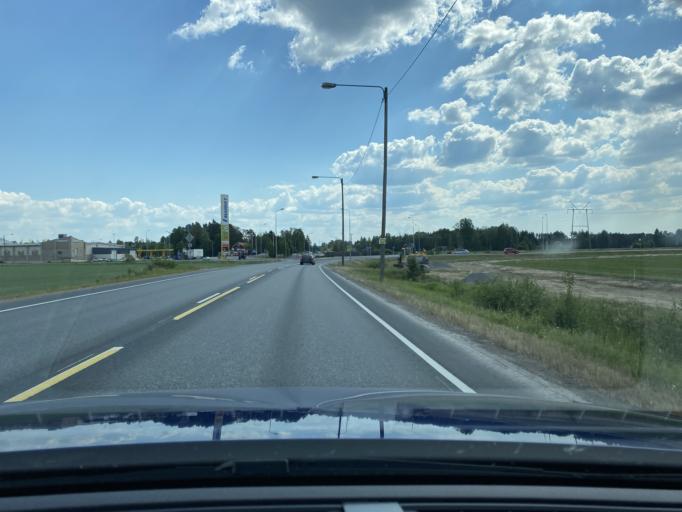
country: FI
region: Satakunta
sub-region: Rauma
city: Eura
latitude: 61.1327
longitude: 22.1235
